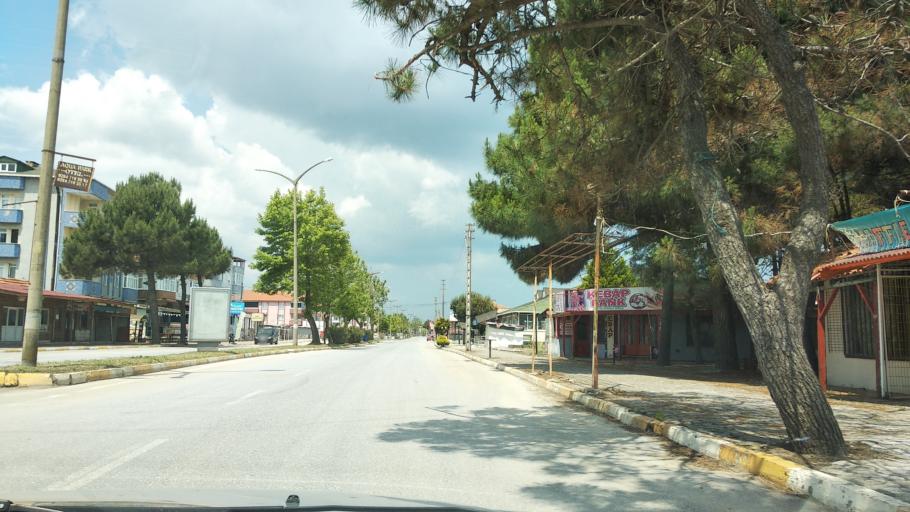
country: TR
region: Sakarya
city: Karasu
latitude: 41.1114
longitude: 30.6894
